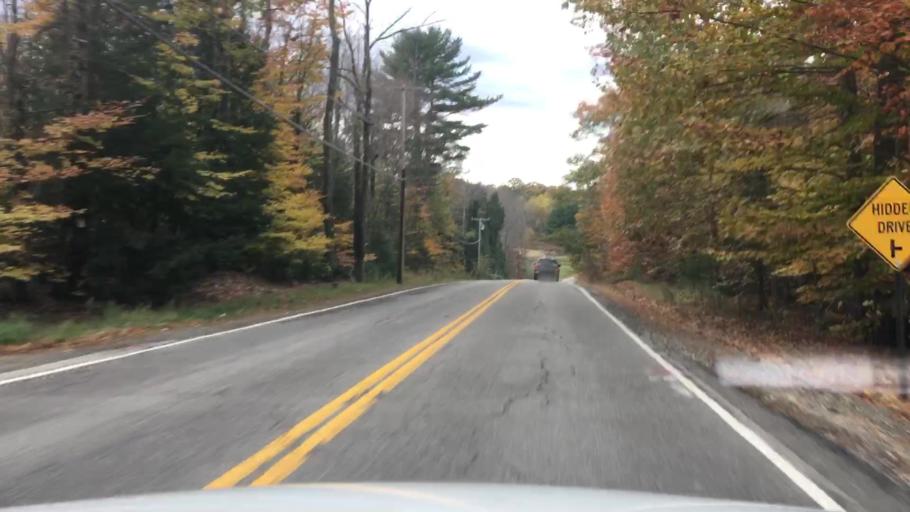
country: US
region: Maine
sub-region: Kennebec County
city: Monmouth
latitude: 44.1347
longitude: -69.9918
